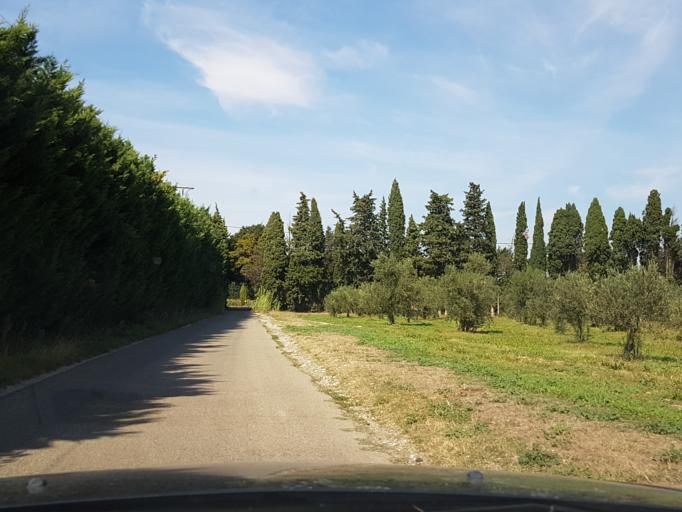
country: FR
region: Provence-Alpes-Cote d'Azur
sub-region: Departement des Bouches-du-Rhone
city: Eygalieres
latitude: 43.7838
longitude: 4.9225
